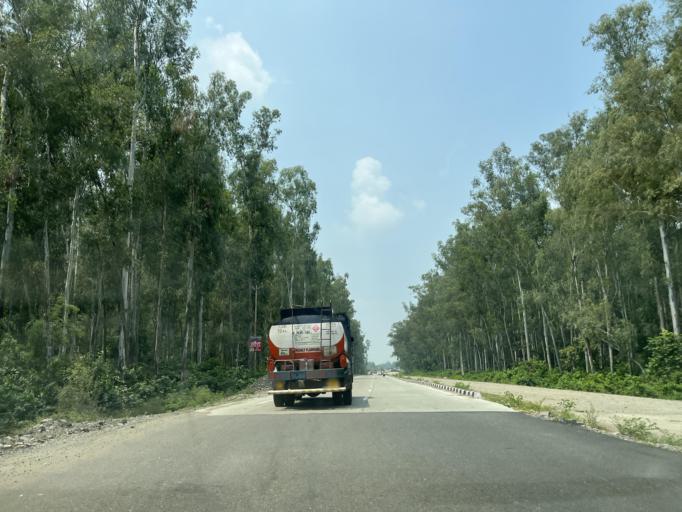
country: IN
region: Uttarakhand
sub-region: Haridwar
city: Sultanpur
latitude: 29.8337
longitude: 78.1999
